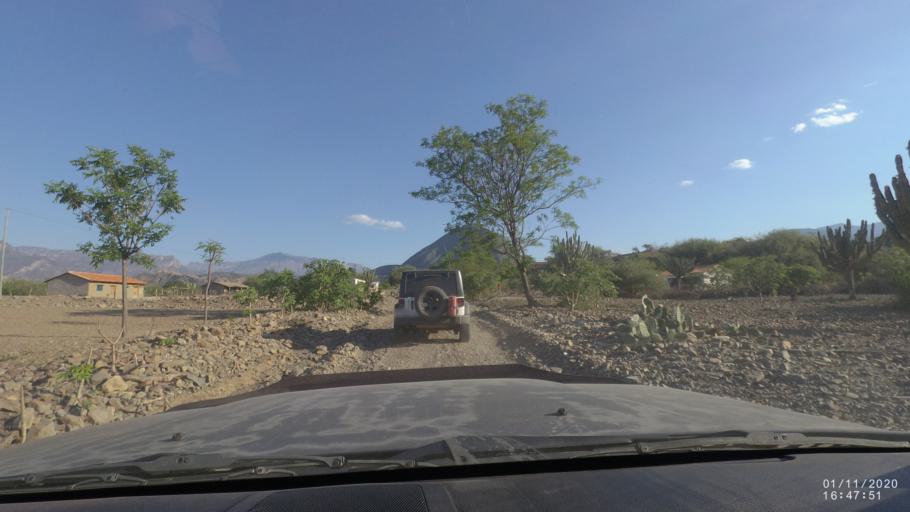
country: BO
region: Chuquisaca
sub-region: Provincia Zudanez
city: Mojocoya
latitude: -18.7272
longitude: -64.5022
